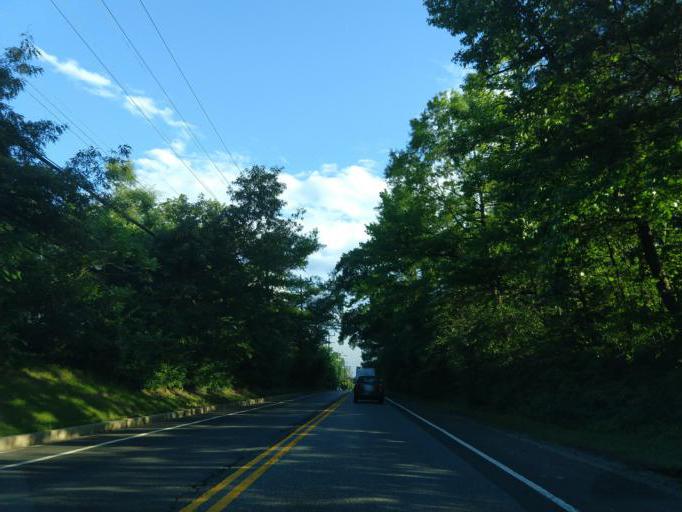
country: US
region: Maryland
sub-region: Prince George's County
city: Berwyn Heights
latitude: 39.0126
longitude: -76.9218
